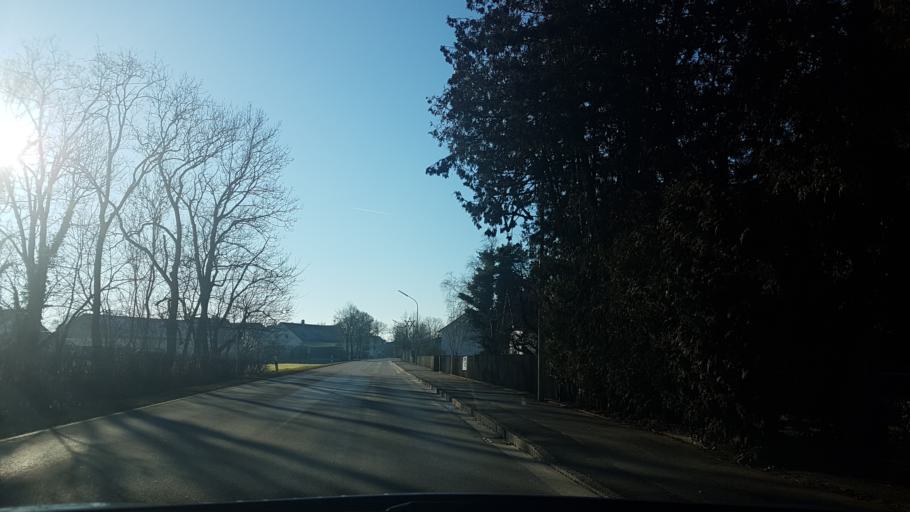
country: DE
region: Bavaria
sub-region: Upper Bavaria
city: Hallbergmoos
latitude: 48.3136
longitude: 11.7590
